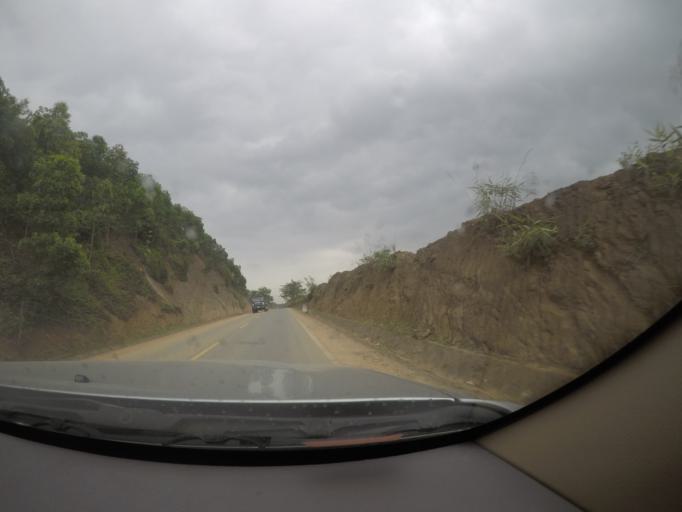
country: VN
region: Quang Binh
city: Ba Don
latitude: 17.6165
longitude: 106.3828
